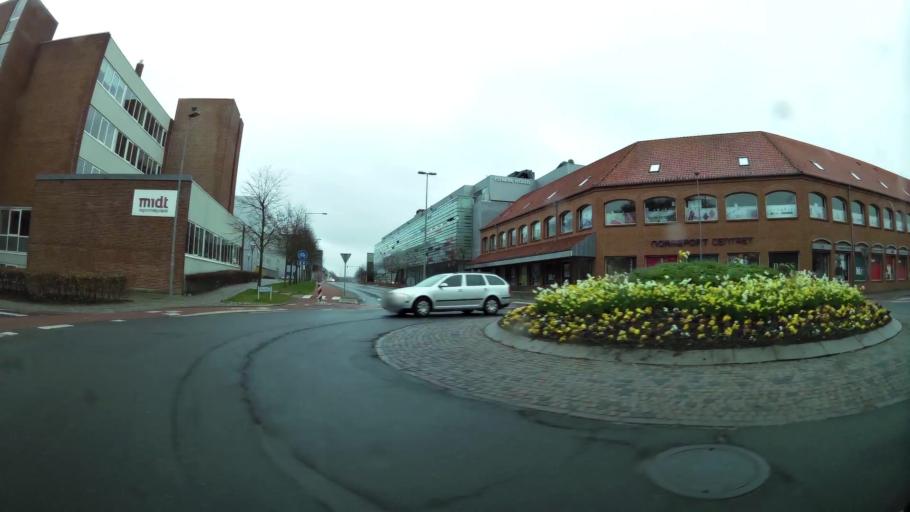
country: DK
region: Central Jutland
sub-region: Holstebro Kommune
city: Holstebro
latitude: 56.3626
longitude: 8.6208
